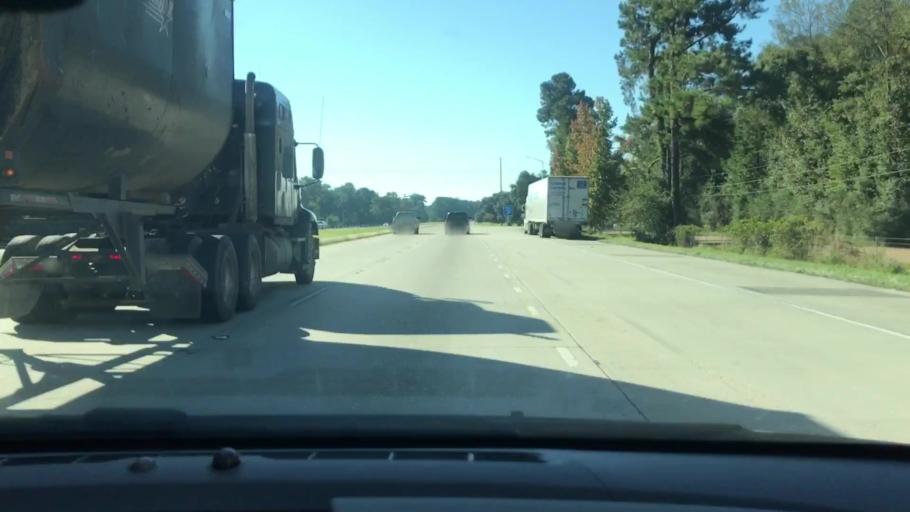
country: US
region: Louisiana
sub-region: Saint Tammany Parish
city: Pearl River
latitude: 30.3249
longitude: -89.7378
